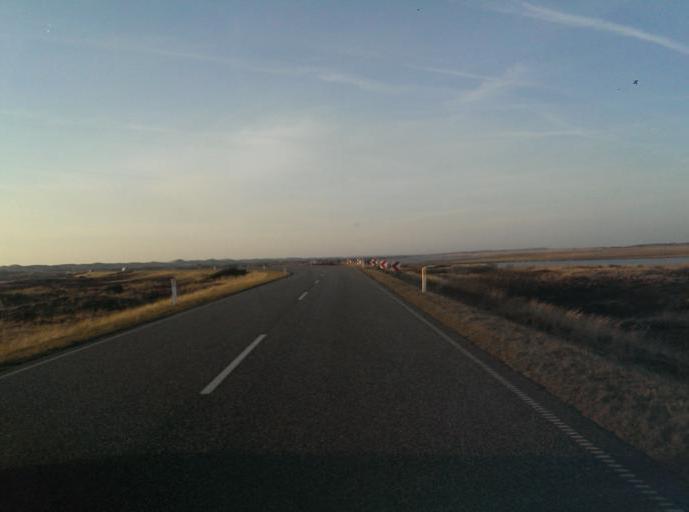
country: DK
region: Central Jutland
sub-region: Ringkobing-Skjern Kommune
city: Hvide Sande
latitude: 55.8209
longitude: 8.1814
